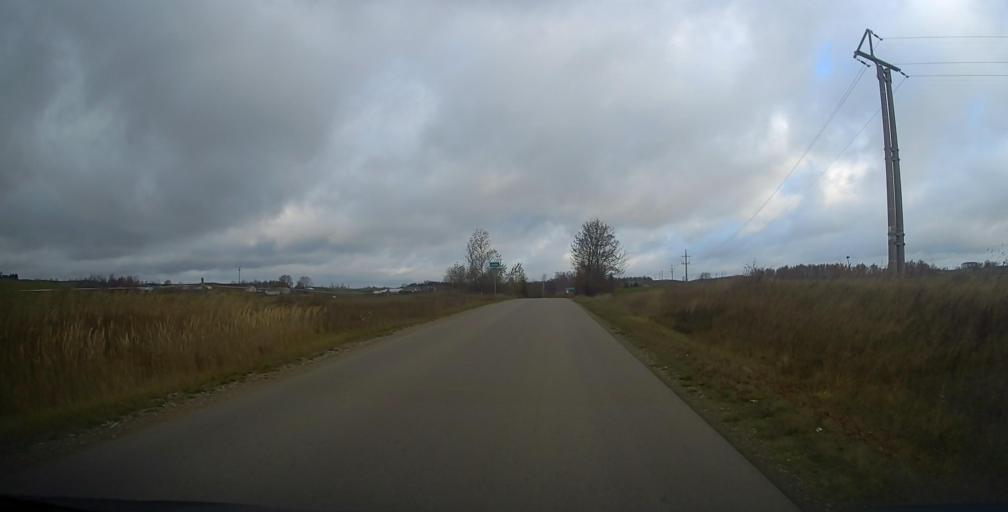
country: PL
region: Podlasie
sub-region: Suwalki
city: Suwalki
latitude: 54.3232
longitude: 22.8625
